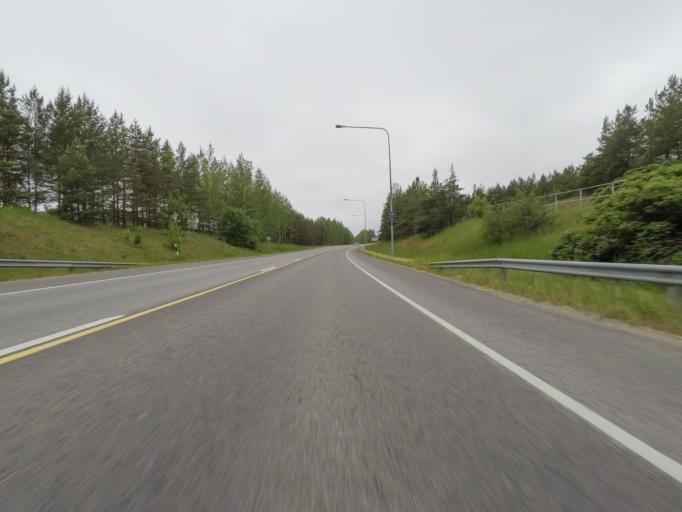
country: FI
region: Varsinais-Suomi
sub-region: Turku
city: Raisio
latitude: 60.4607
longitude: 22.1823
